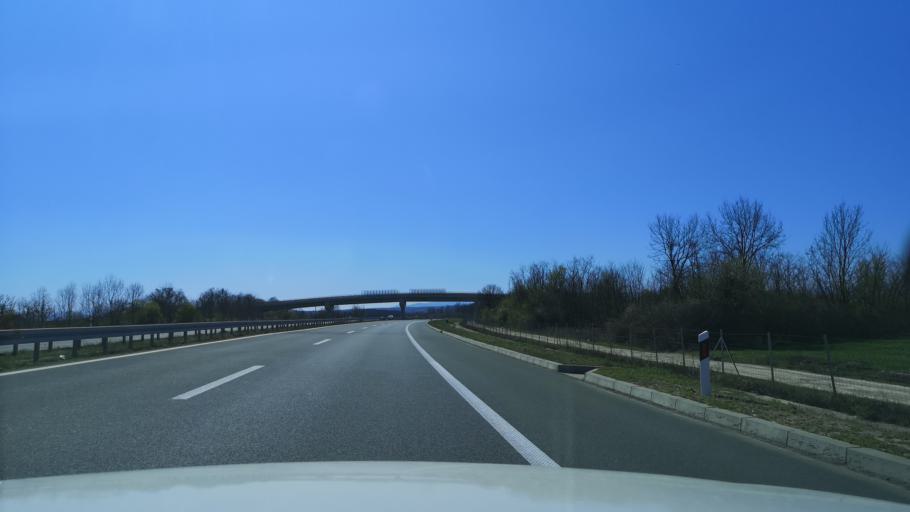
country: RS
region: Central Serbia
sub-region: Kolubarski Okrug
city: Lajkovac
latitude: 44.3807
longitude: 20.1146
